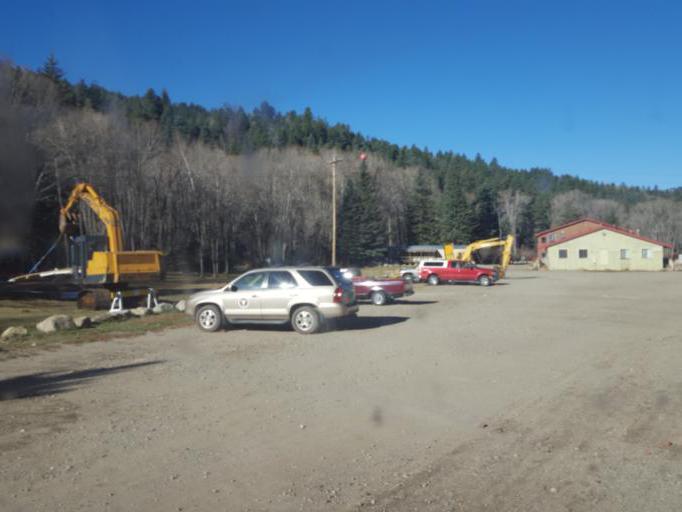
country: US
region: New Mexico
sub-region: Taos County
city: Ranchos de Taos
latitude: 36.1544
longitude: -105.5488
